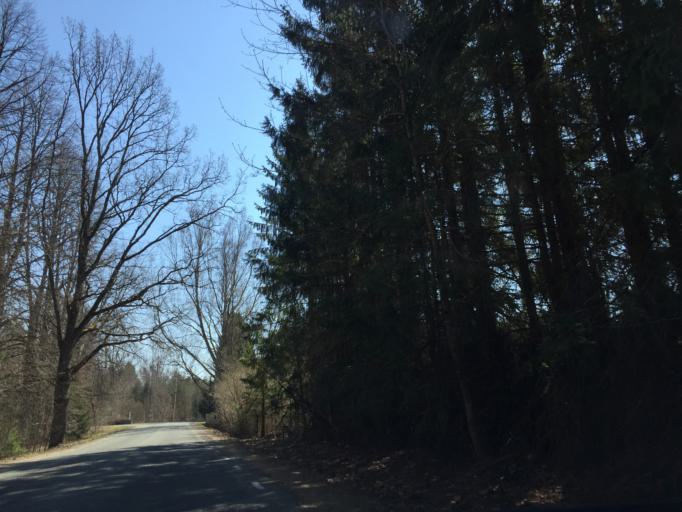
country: EE
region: Jogevamaa
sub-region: Mustvee linn
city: Mustvee
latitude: 58.5853
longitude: 26.8988
